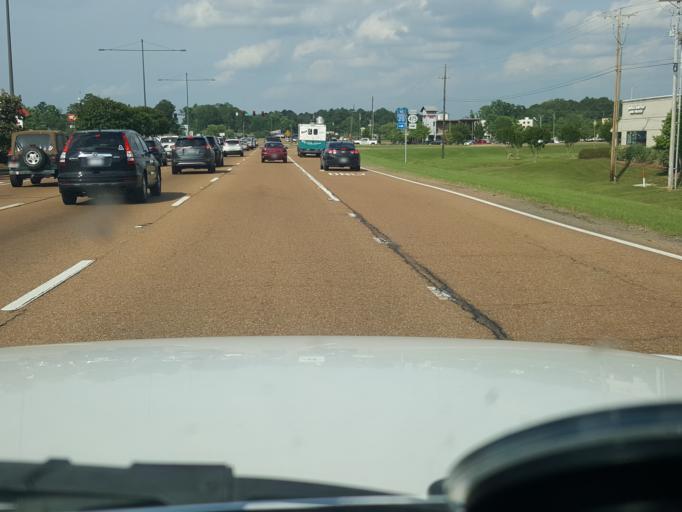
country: US
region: Mississippi
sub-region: Rankin County
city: Flowood
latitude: 32.3369
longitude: -90.0947
